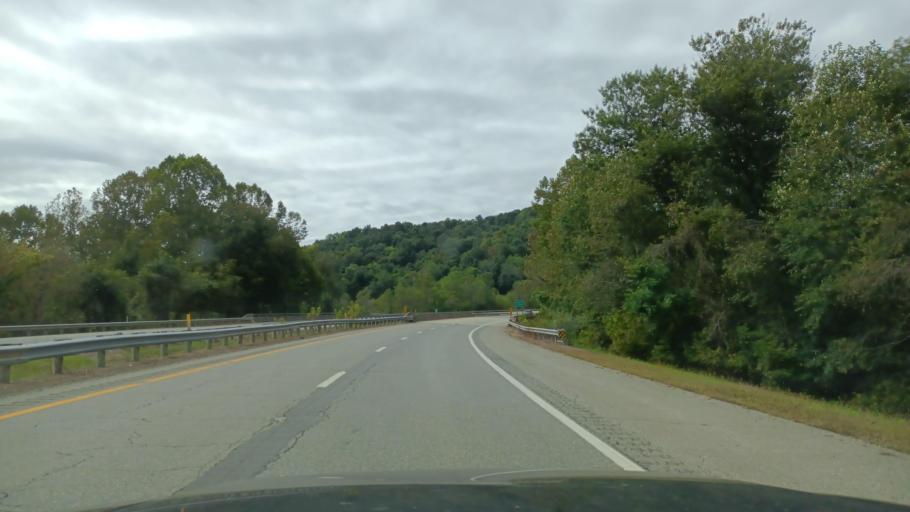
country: US
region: Ohio
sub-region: Washington County
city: Newport
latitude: 39.2388
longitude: -81.2229
